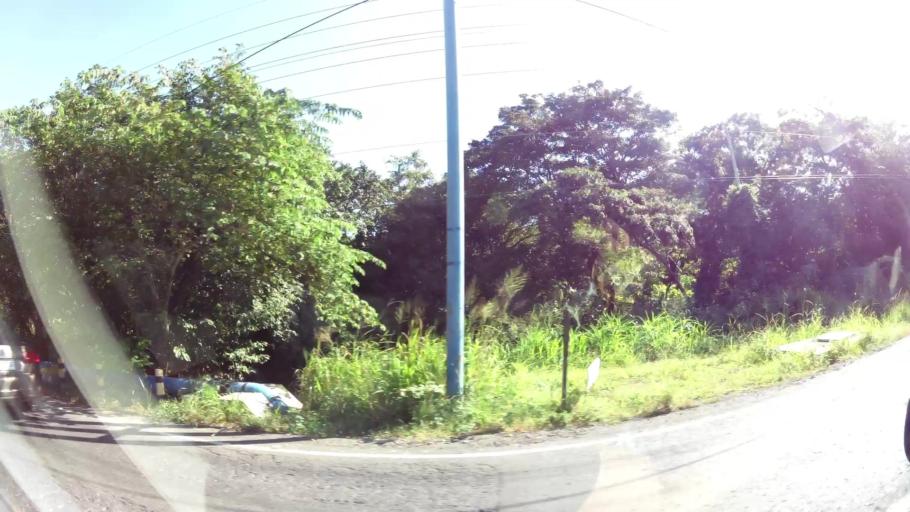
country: CR
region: Guanacaste
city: Liberia
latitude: 10.6137
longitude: -85.4855
